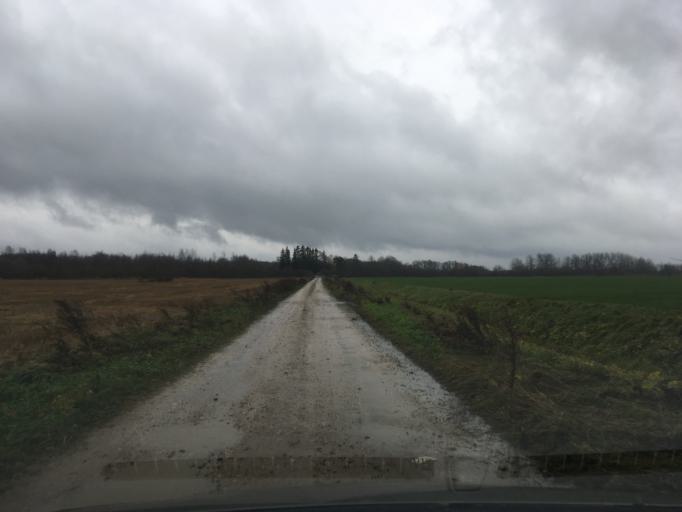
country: EE
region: Laeaene
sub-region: Lihula vald
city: Lihula
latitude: 58.7035
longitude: 23.8547
